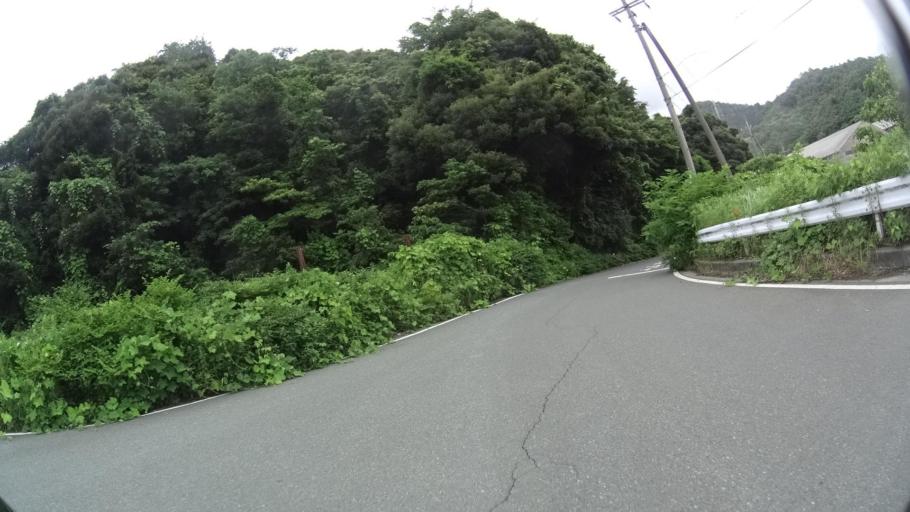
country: JP
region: Kyoto
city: Maizuru
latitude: 35.4993
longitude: 135.3879
